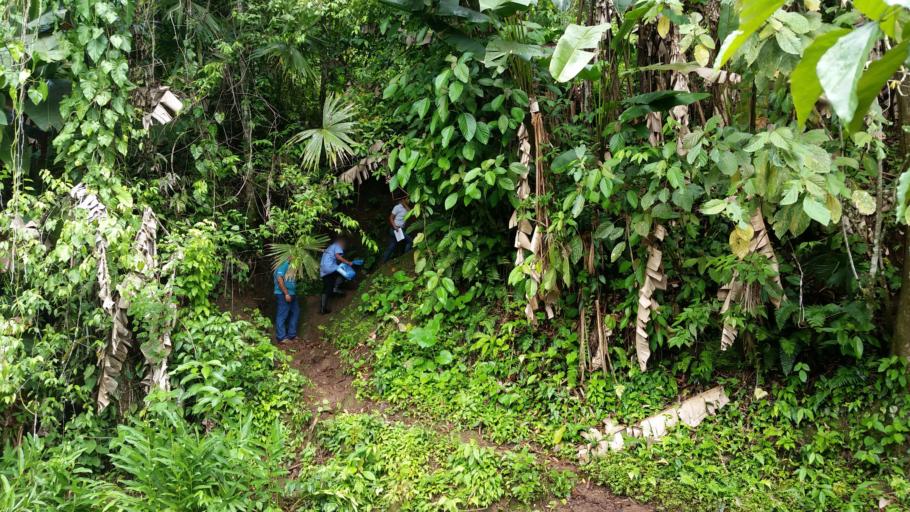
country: NI
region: Atlantico Norte (RAAN)
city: Waslala
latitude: 13.1664
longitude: -85.4007
